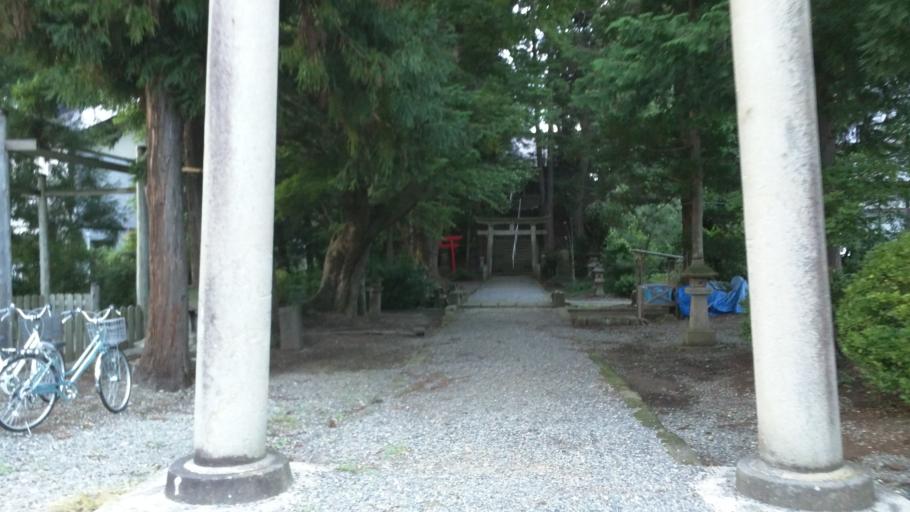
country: JP
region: Fukushima
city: Kitakata
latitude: 37.5087
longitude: 139.9446
